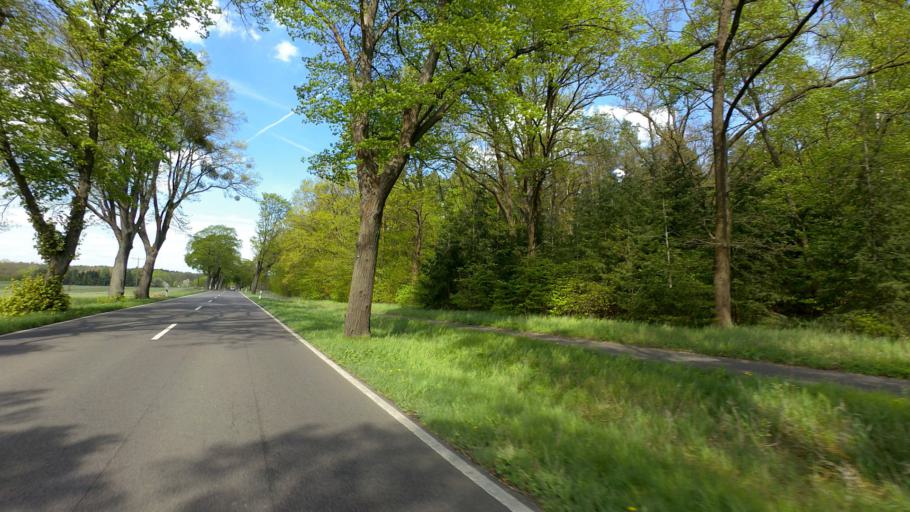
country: DE
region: Brandenburg
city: Milmersdorf
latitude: 53.0686
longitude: 13.6233
